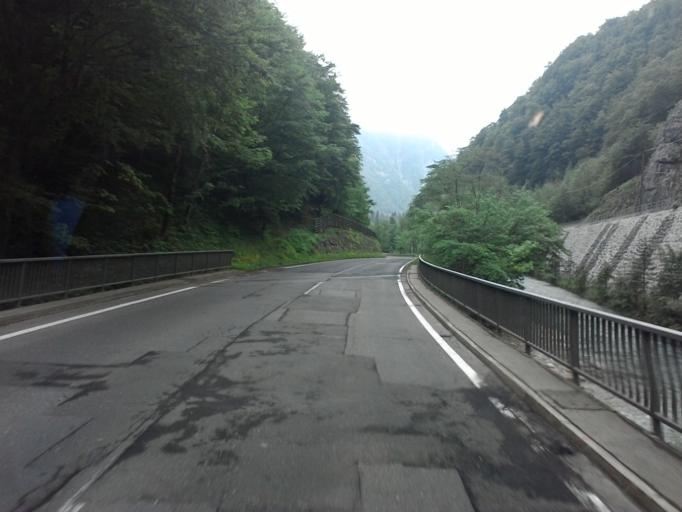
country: AT
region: Styria
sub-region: Politischer Bezirk Leoben
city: Hieflau
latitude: 47.5908
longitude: 14.7529
